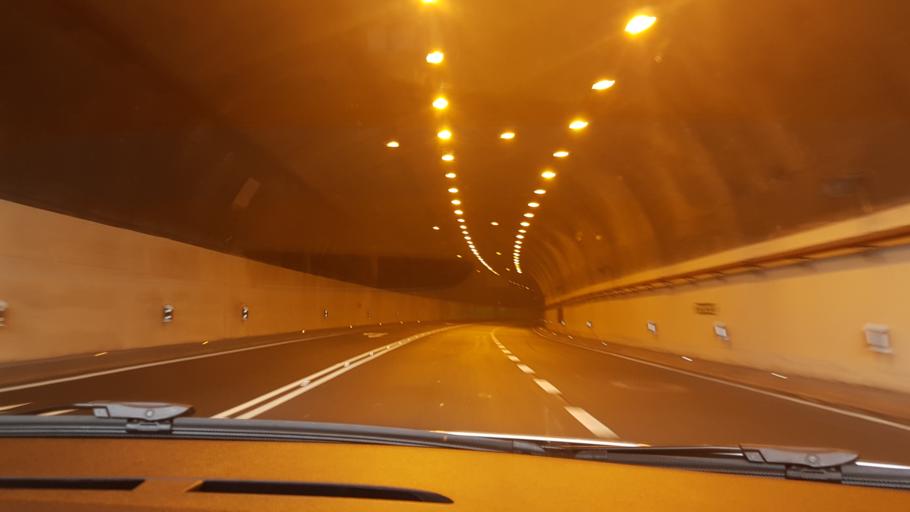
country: PT
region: Madeira
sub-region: Santana
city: Santana
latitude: 32.8093
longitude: -16.8740
